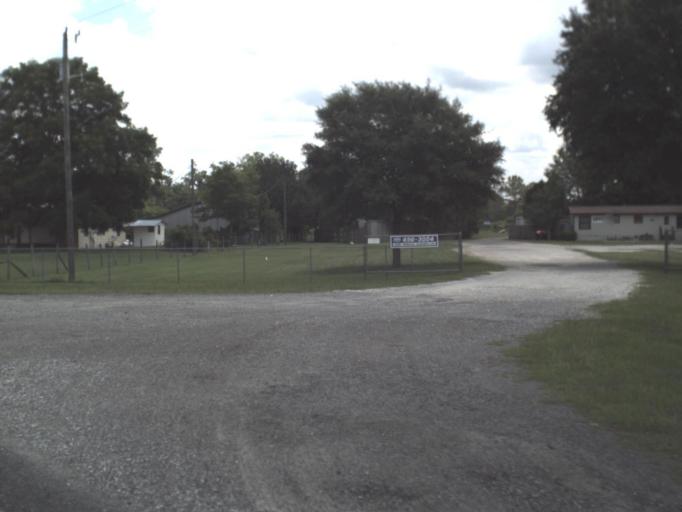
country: US
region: Florida
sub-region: Union County
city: Lake Butler
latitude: 30.0030
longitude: -82.3693
